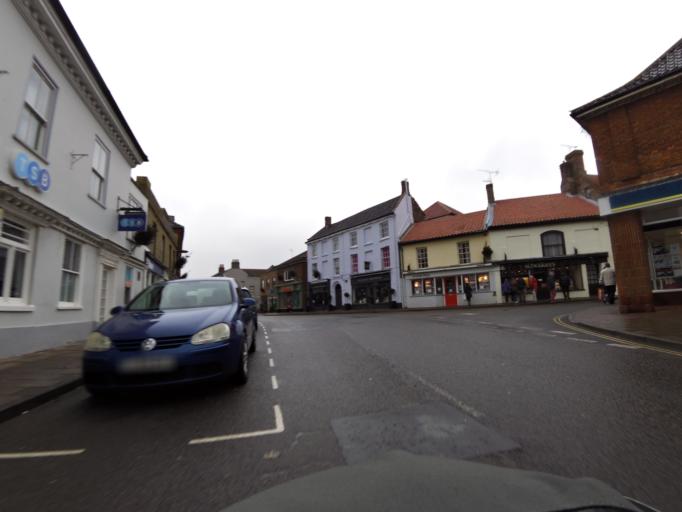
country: GB
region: England
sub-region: Norfolk
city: Briston
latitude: 52.9060
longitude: 1.0888
